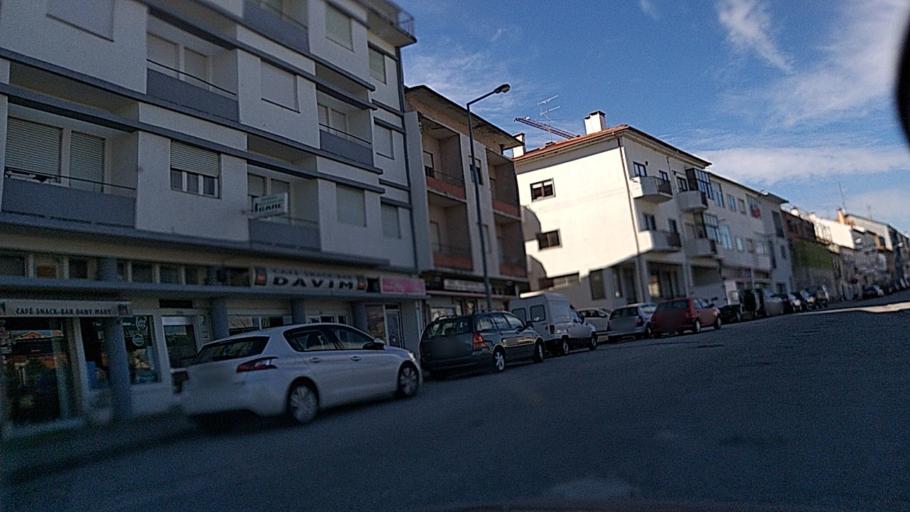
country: PT
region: Guarda
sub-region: Guarda
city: Sequeira
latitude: 40.5528
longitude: -7.2405
